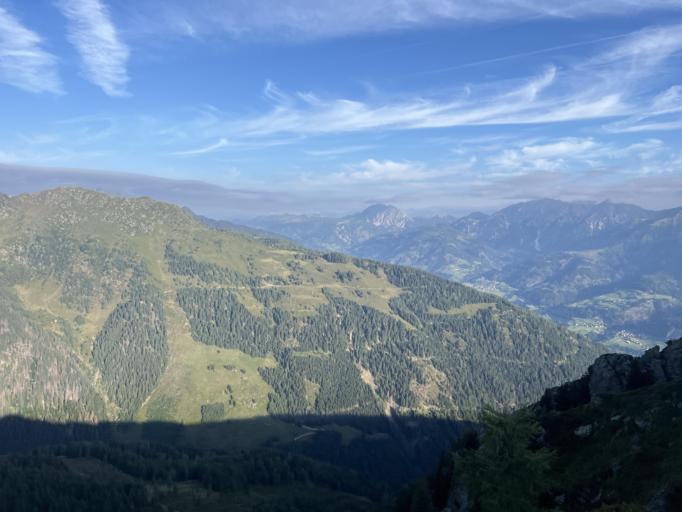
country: IT
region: Friuli Venezia Giulia
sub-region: Provincia di Udine
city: Rigolato
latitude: 46.6506
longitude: 12.8486
